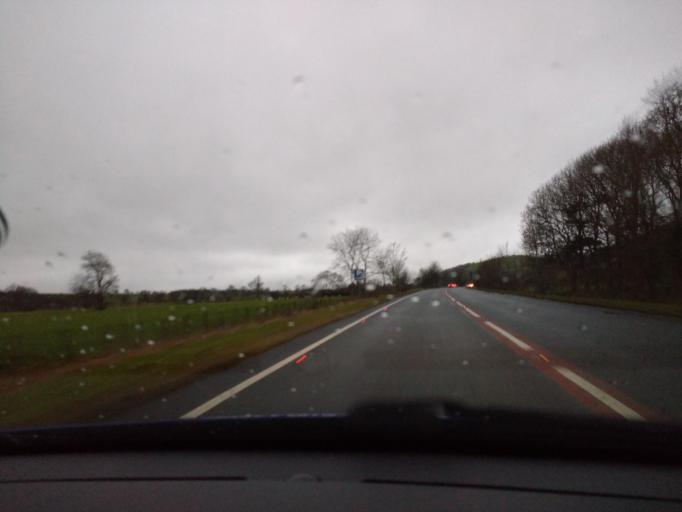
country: GB
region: England
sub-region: Cumbria
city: Cockermouth
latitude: 54.6595
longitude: -3.3005
